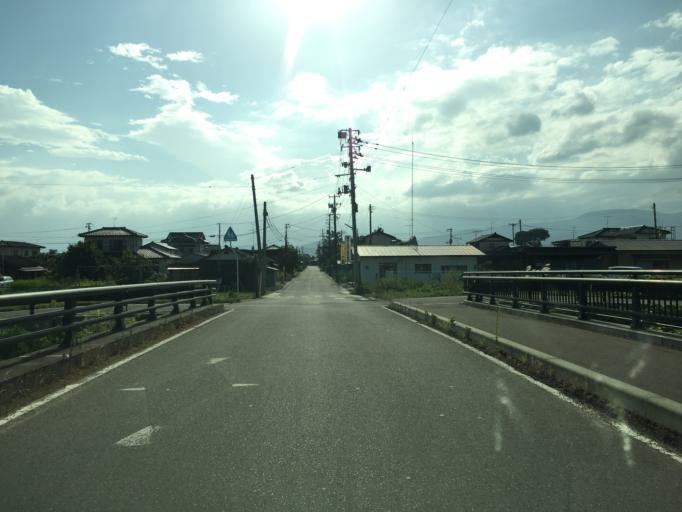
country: JP
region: Fukushima
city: Yanagawamachi-saiwaicho
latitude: 37.8536
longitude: 140.5968
